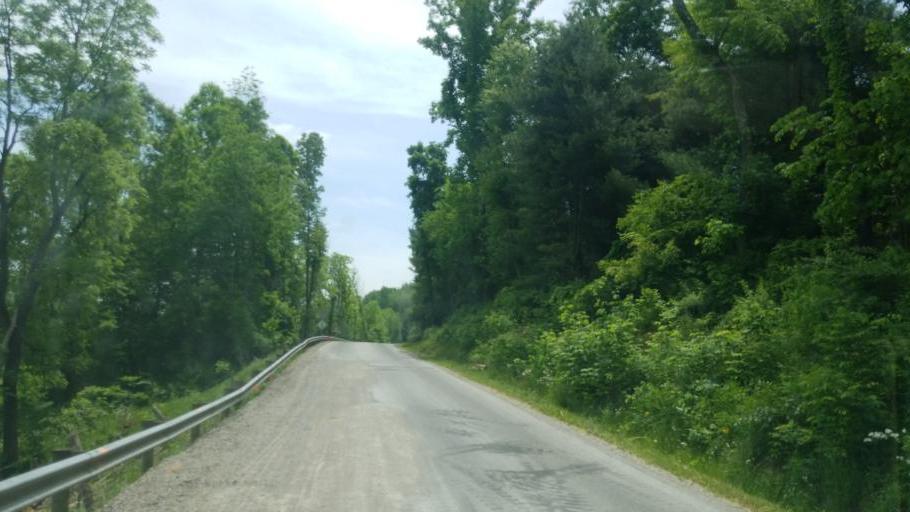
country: US
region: Ohio
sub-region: Coshocton County
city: West Lafayette
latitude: 40.3918
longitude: -81.7616
